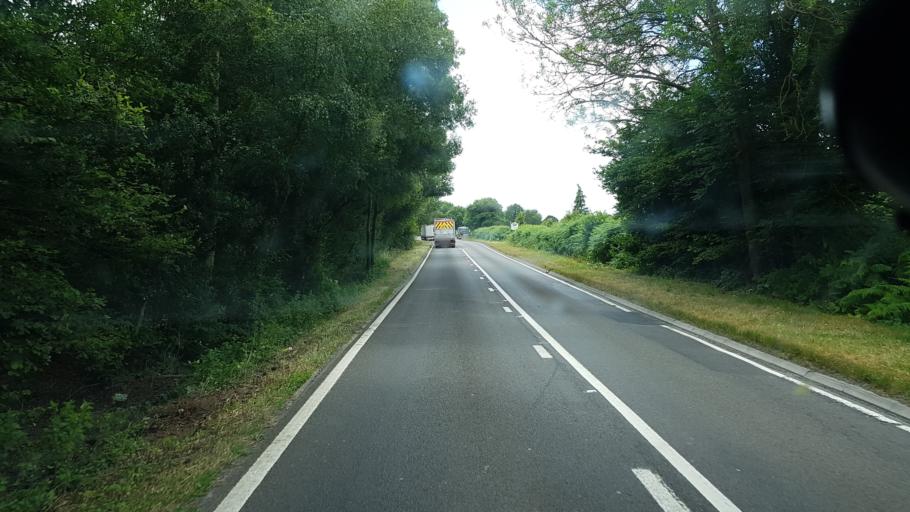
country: GB
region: England
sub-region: Surrey
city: Lingfield
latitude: 51.1778
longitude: -0.0473
